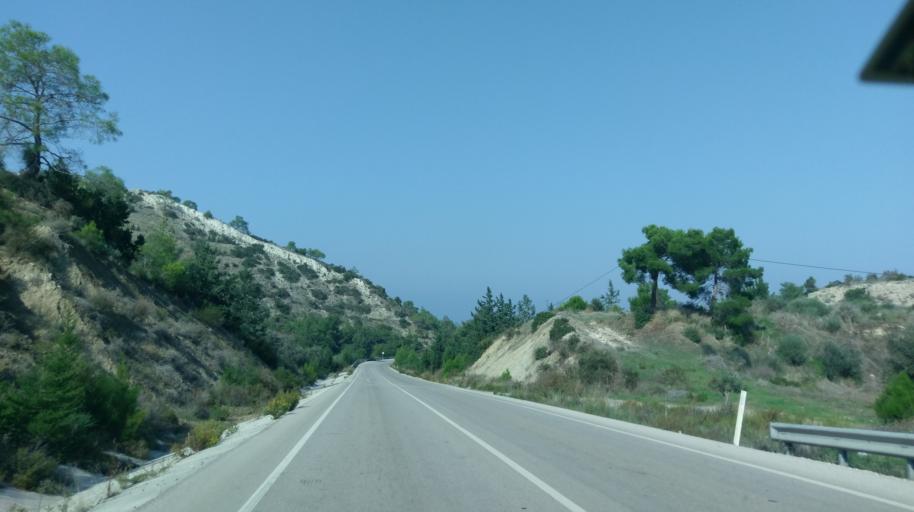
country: CY
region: Ammochostos
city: Lefkonoiko
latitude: 35.3617
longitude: 33.7110
